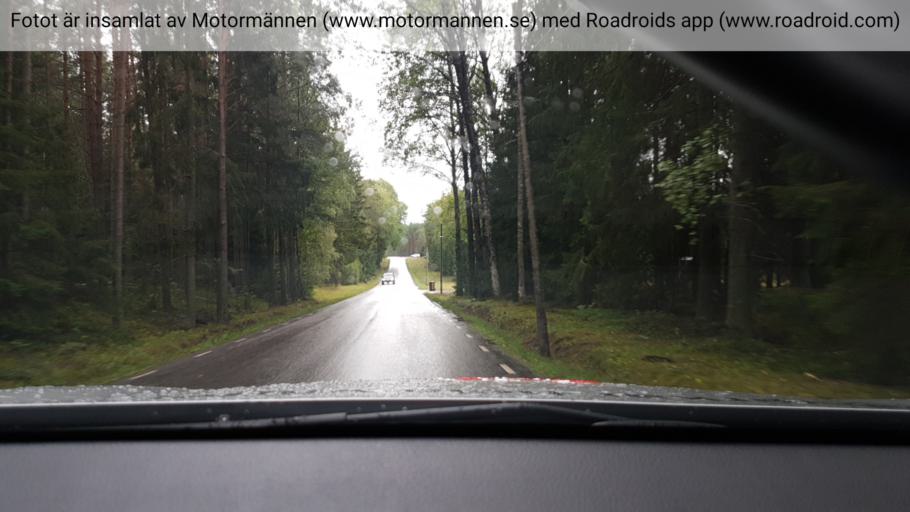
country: SE
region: Stockholm
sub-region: Haninge Kommun
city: Jordbro
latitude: 59.0885
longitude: 18.0448
